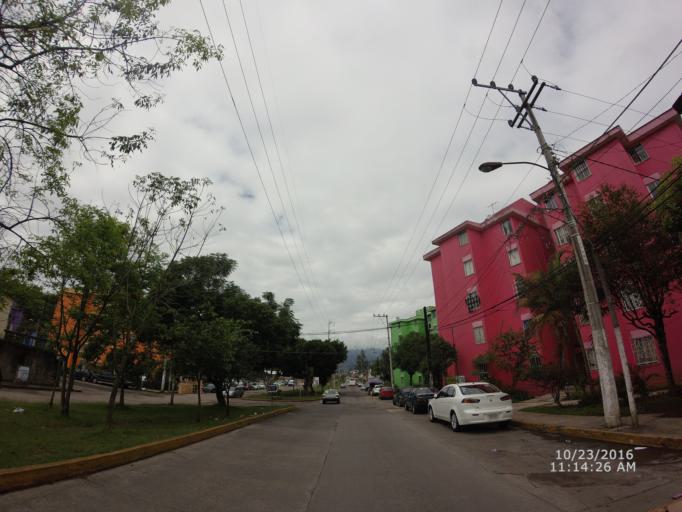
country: MX
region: Veracruz
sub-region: Tlalnelhuayocan
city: Guadalupe Victoria
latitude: 19.5503
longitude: -96.9408
